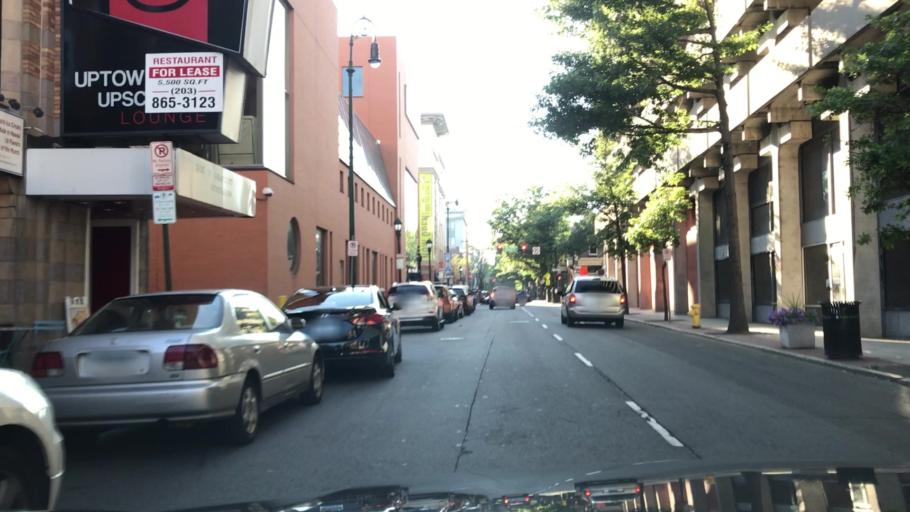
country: US
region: Connecticut
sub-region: New Haven County
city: New Haven
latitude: 41.3056
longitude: -72.9288
